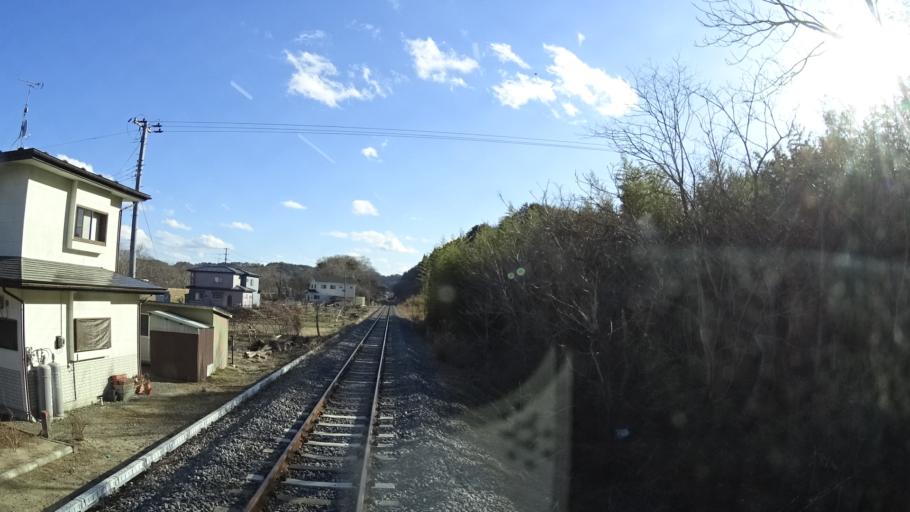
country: JP
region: Iwate
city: Miyako
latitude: 39.5732
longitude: 141.9334
